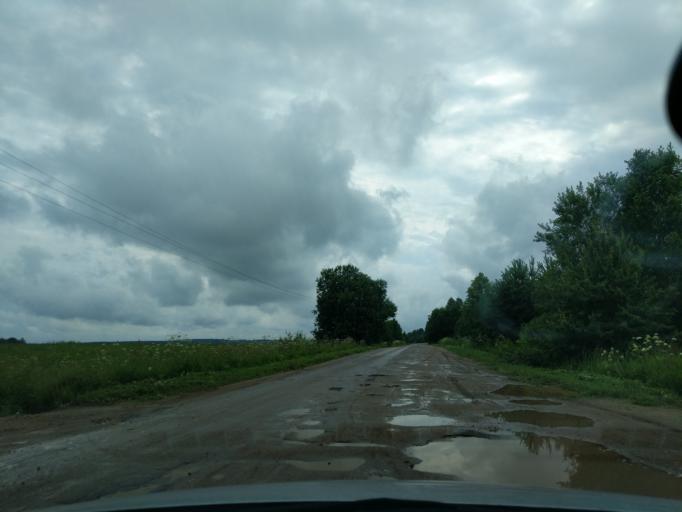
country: RU
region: Kaluga
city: Nikola-Lenivets
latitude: 54.7760
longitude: 35.7210
